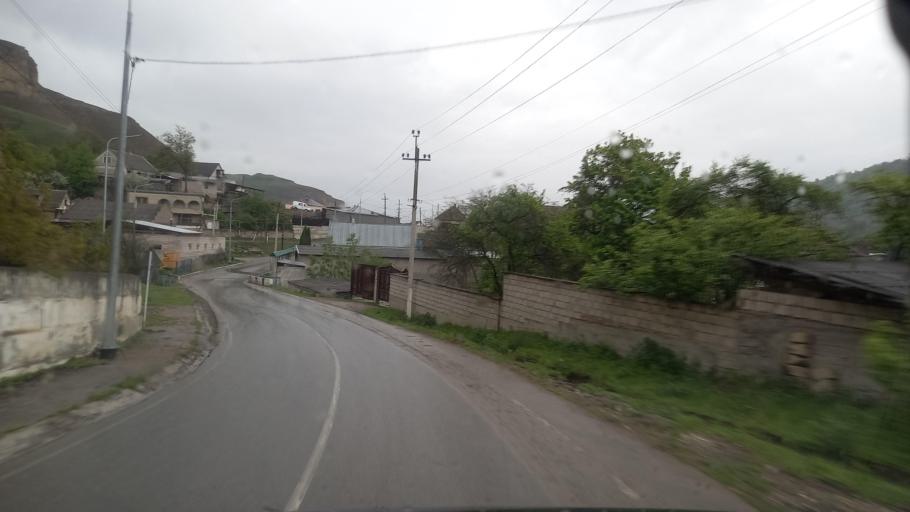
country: RU
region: Kabardino-Balkariya
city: Gundelen
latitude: 43.5997
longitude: 43.1537
